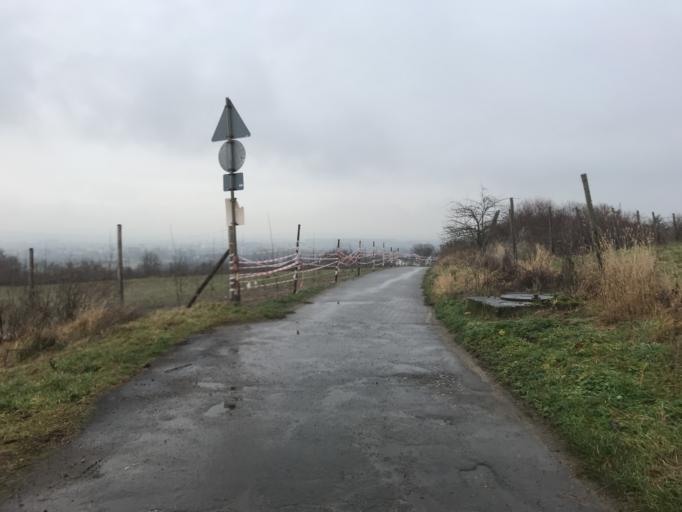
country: DE
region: Rheinland-Pfalz
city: Wackernheim
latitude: 49.9901
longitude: 8.1004
